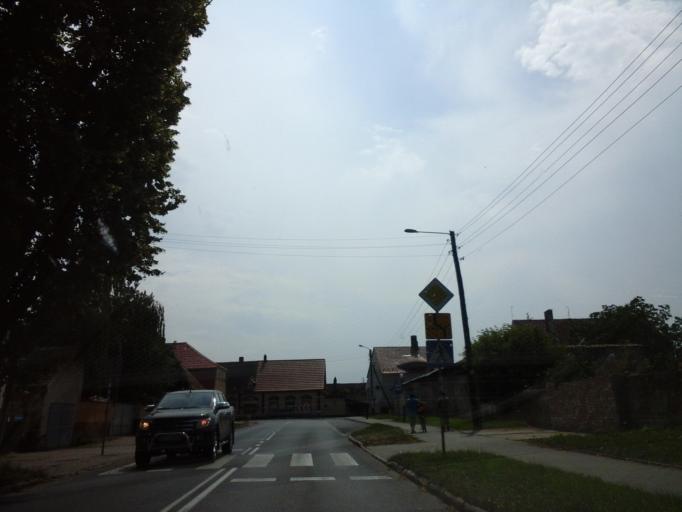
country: PL
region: Lower Silesian Voivodeship
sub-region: Powiat strzelinski
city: Strzelin
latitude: 50.8679
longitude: 17.0661
